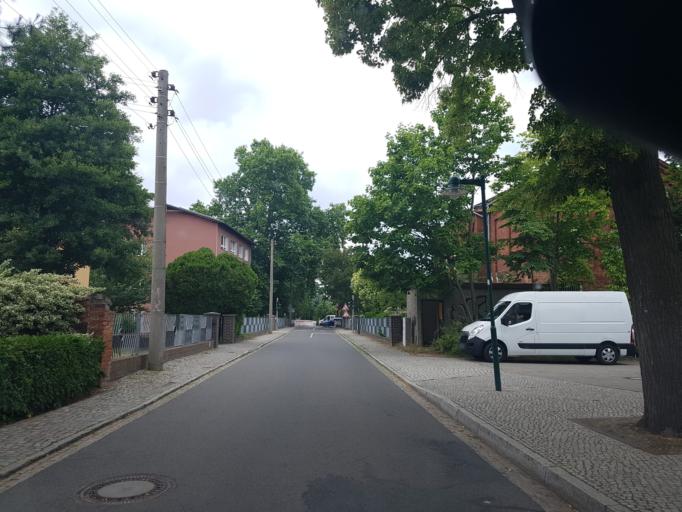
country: DE
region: Brandenburg
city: Treuenbrietzen
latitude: 52.0992
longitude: 12.8784
